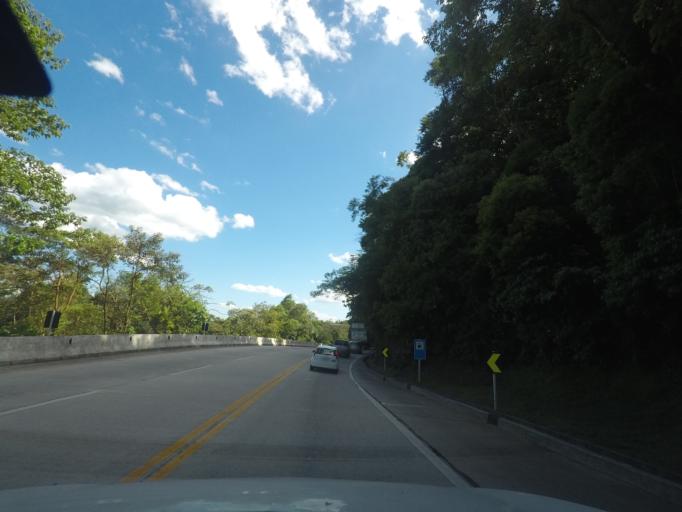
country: BR
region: Rio de Janeiro
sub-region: Guapimirim
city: Guapimirim
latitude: -22.4786
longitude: -42.9958
